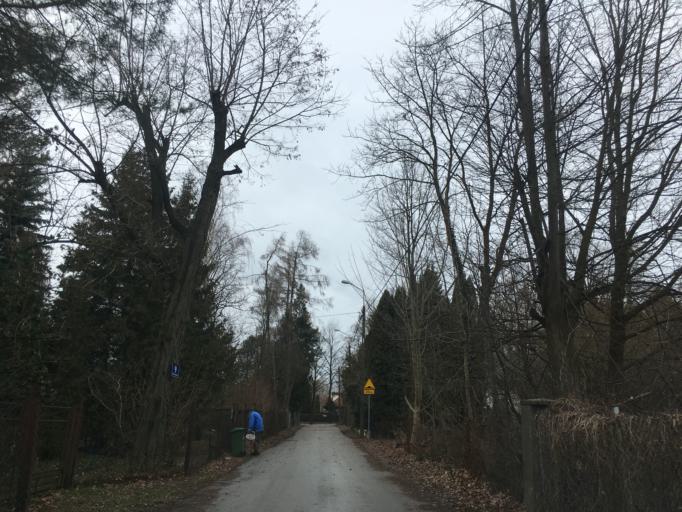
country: PL
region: Masovian Voivodeship
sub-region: Powiat piaseczynski
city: Lesznowola
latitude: 52.0334
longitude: 20.9592
